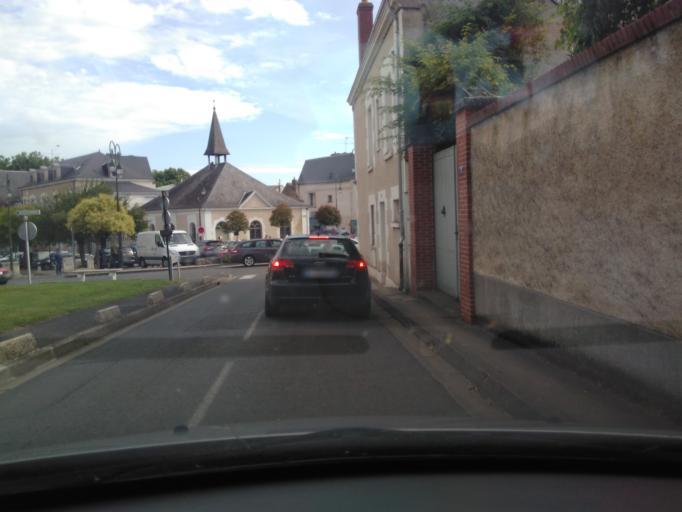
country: FR
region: Centre
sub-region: Departement d'Indre-et-Loire
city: Amboise
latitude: 47.4102
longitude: 0.9795
